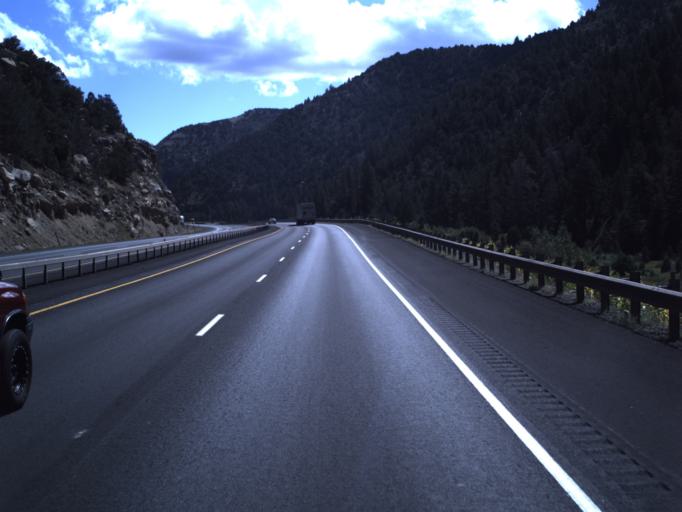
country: US
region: Utah
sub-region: Sevier County
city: Salina
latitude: 38.8878
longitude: -111.6098
